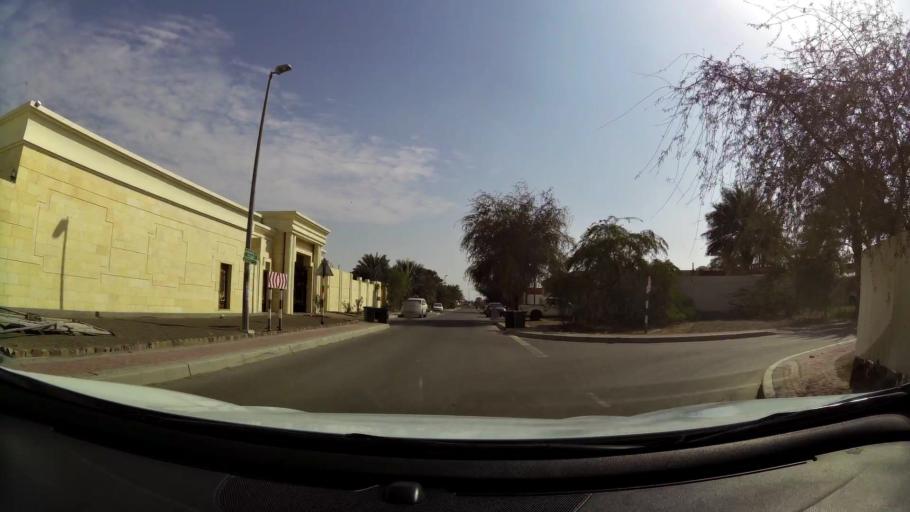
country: AE
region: Abu Dhabi
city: Al Ain
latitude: 24.0966
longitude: 55.9229
